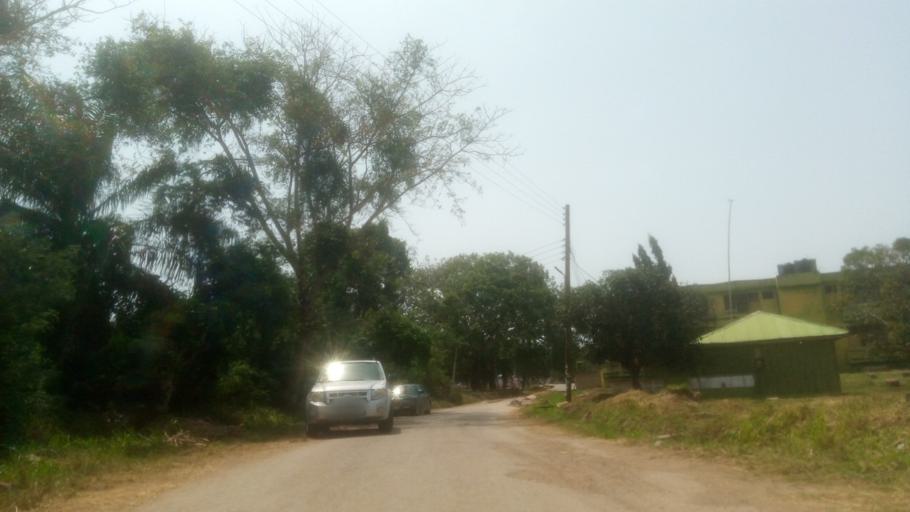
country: GH
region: Central
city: Winneba
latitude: 5.3646
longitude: -0.6333
